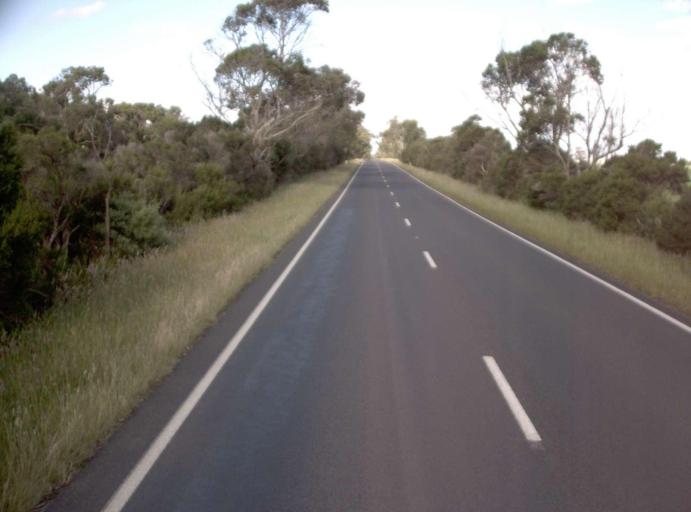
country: AU
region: Victoria
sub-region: Bass Coast
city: North Wonthaggi
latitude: -38.5952
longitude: 145.7889
